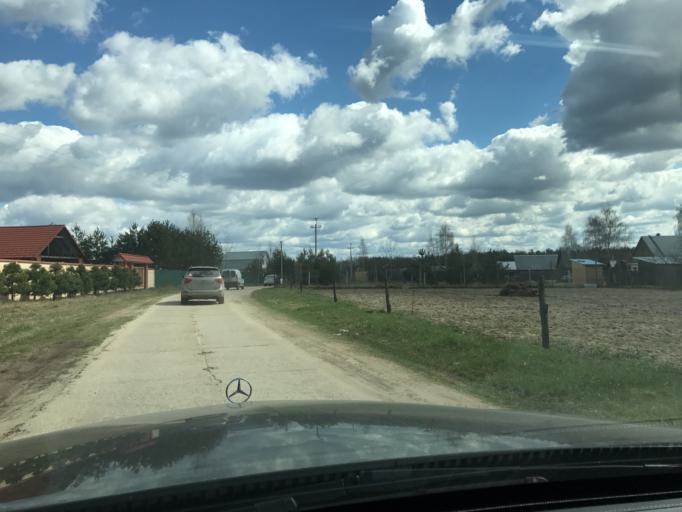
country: RU
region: Vladimir
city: Pokrov
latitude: 55.8518
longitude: 39.1906
